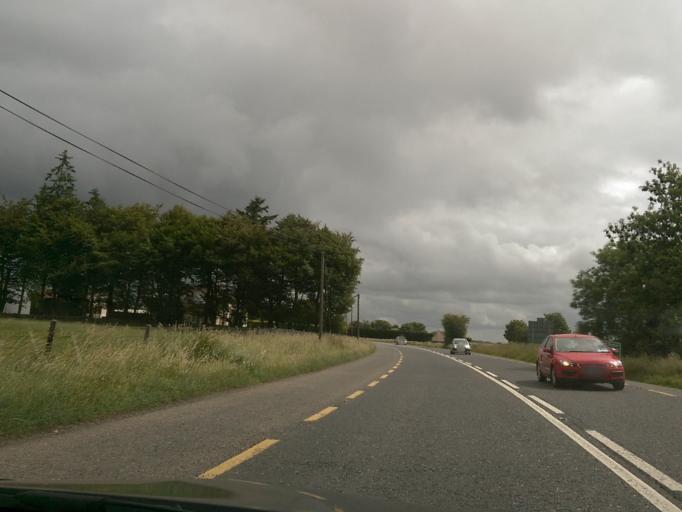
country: IE
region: Connaught
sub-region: County Galway
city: Loughrea
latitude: 53.2090
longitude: -8.5162
